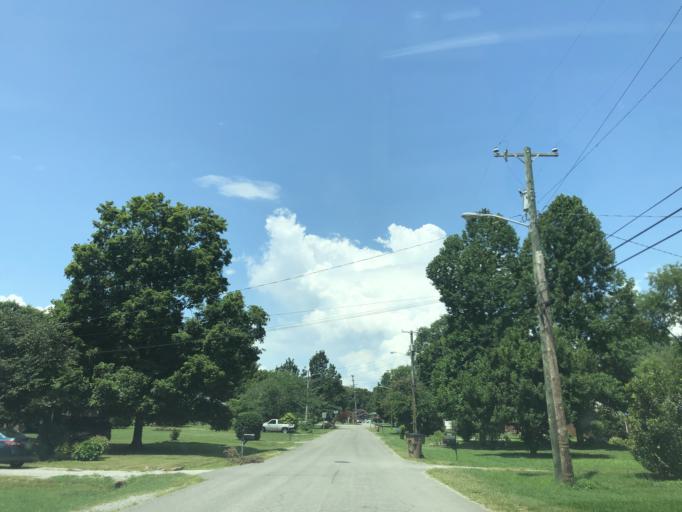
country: US
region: Tennessee
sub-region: Davidson County
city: Lakewood
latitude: 36.1554
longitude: -86.6603
